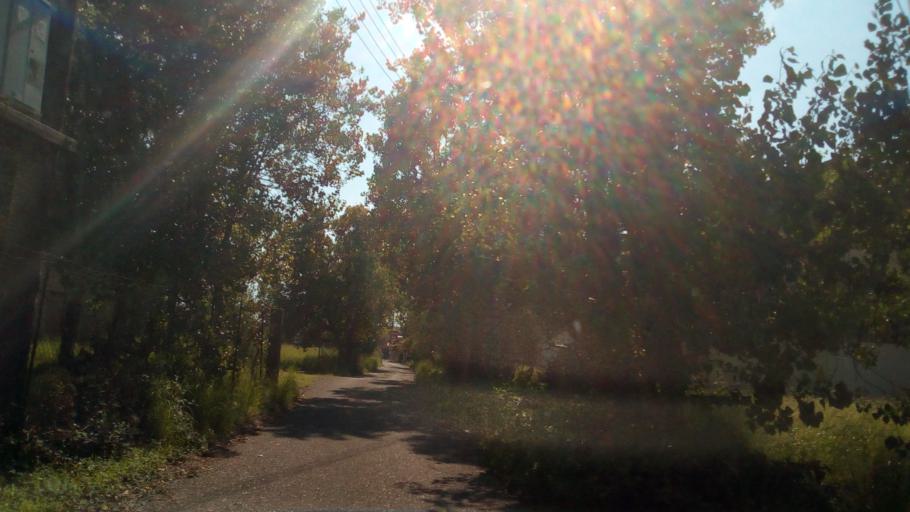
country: GR
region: West Greece
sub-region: Nomos Aitolias kai Akarnanias
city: Nafpaktos
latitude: 38.4014
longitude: 21.8435
